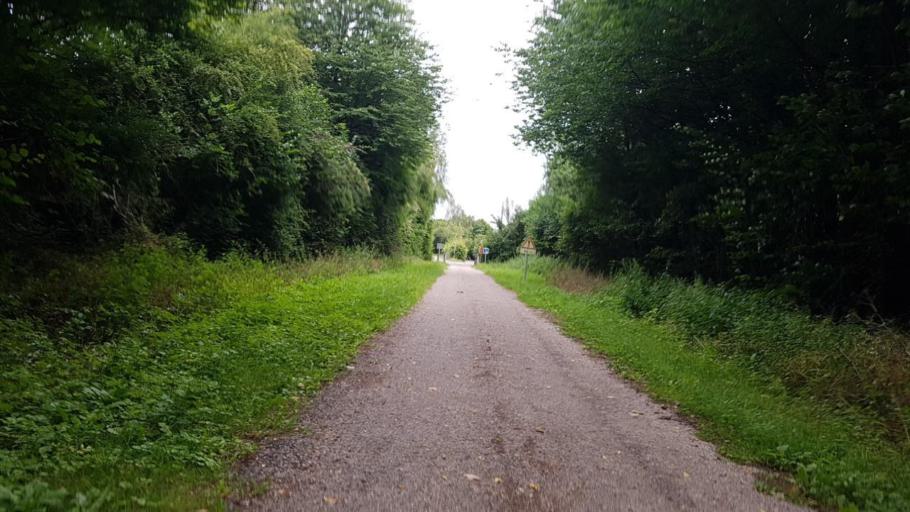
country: FR
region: Picardie
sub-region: Departement de l'Aisne
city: Origny-en-Thierache
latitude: 49.9277
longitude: 4.0333
